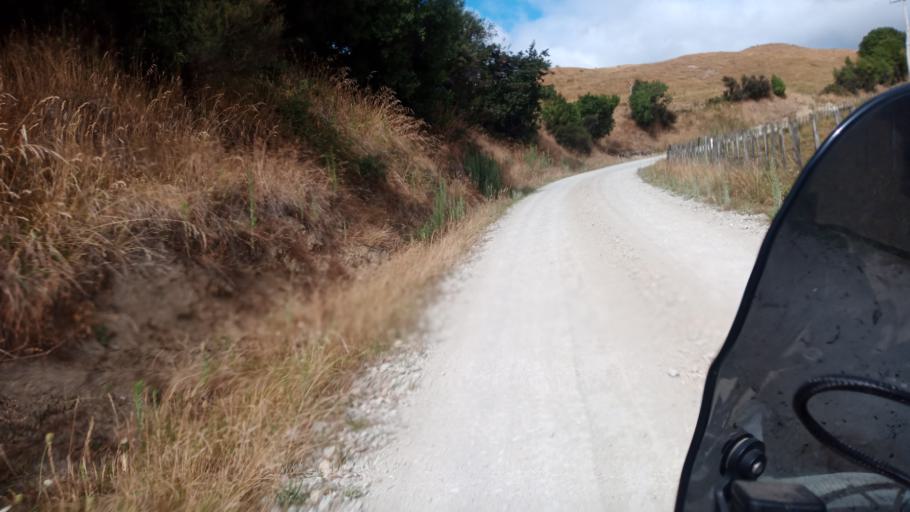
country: NZ
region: Hawke's Bay
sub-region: Wairoa District
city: Wairoa
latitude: -38.6033
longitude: 177.4796
